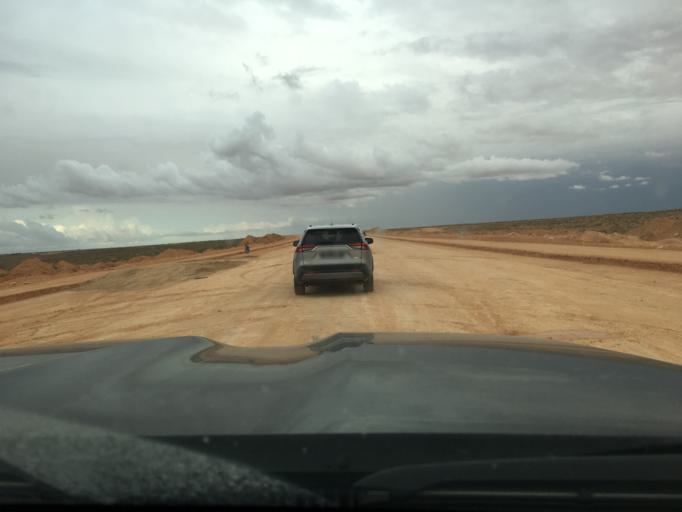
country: TN
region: Madanin
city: Medenine
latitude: 33.2670
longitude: 10.5835
